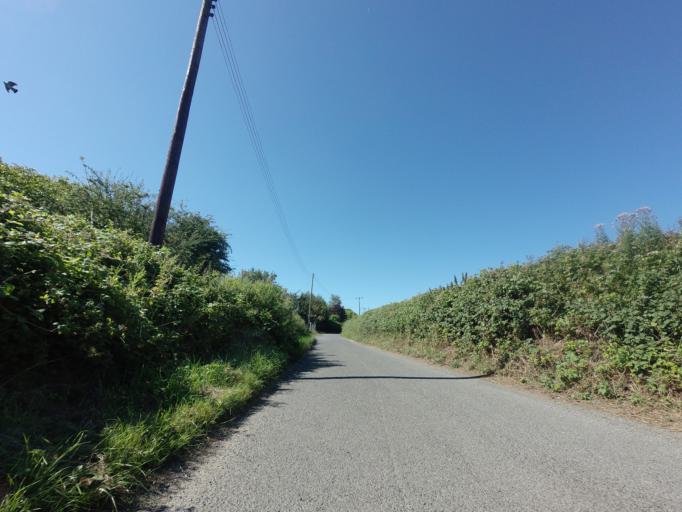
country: GB
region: England
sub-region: Kent
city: Ash
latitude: 51.3007
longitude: 1.2391
